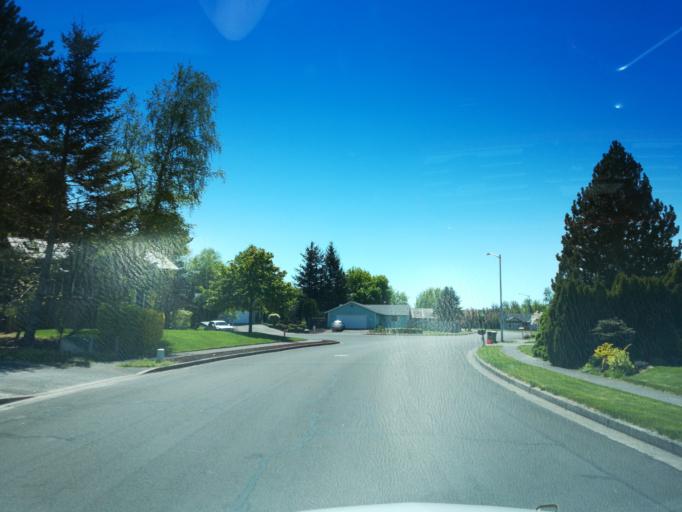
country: US
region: Oregon
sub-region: Multnomah County
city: Troutdale
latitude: 45.5276
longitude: -122.3749
